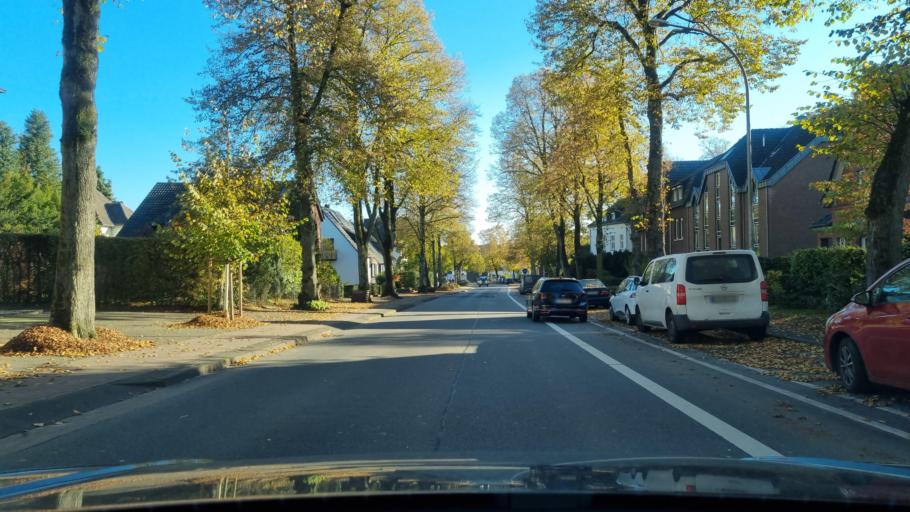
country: DE
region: North Rhine-Westphalia
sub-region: Regierungsbezirk Dusseldorf
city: Kleve
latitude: 51.7874
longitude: 6.1228
